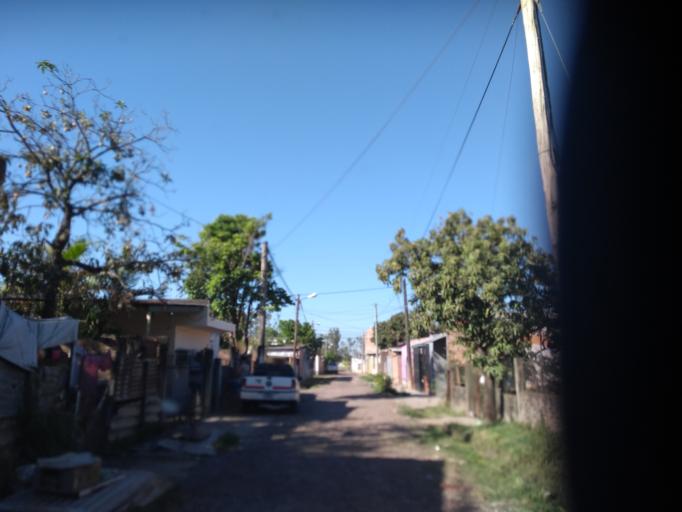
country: AR
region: Chaco
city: Resistencia
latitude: -27.4684
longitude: -58.9763
